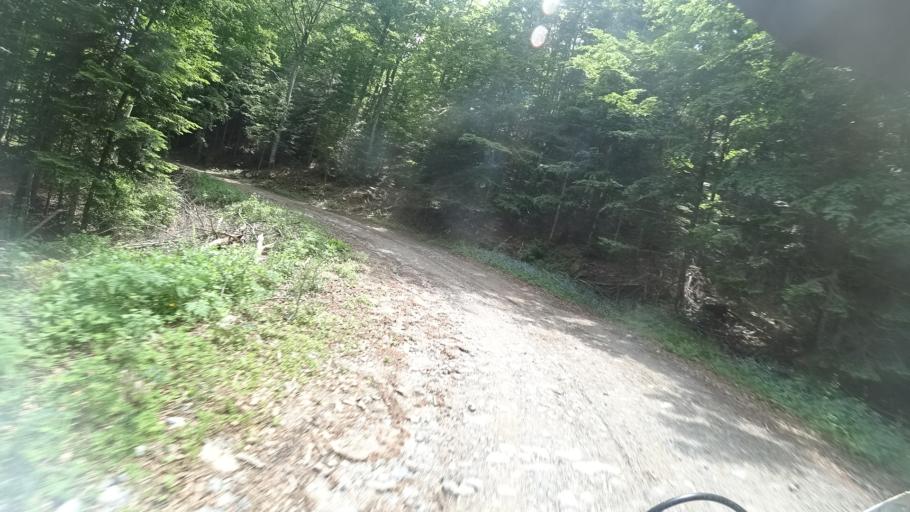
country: HR
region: Zadarska
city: Gracac
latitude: 44.4911
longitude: 15.8716
